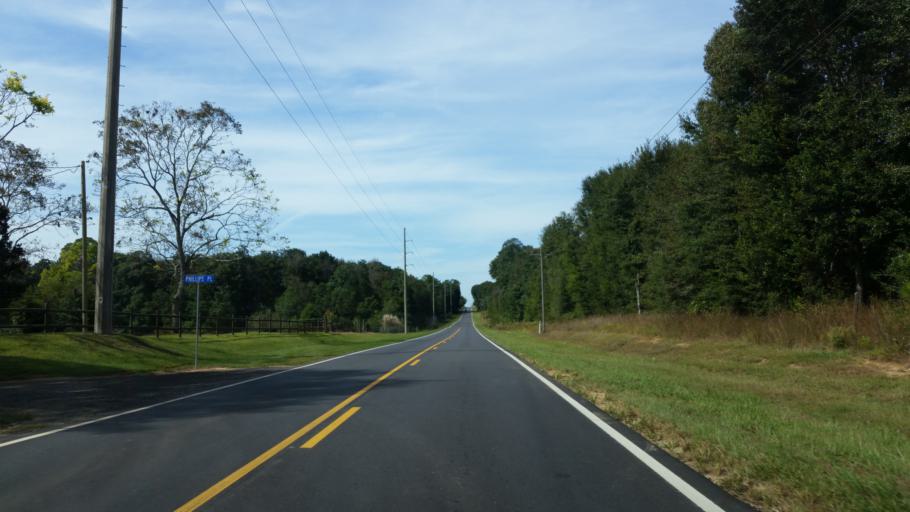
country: US
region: Alabama
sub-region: Baldwin County
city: Loxley
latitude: 30.6331
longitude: -87.6996
